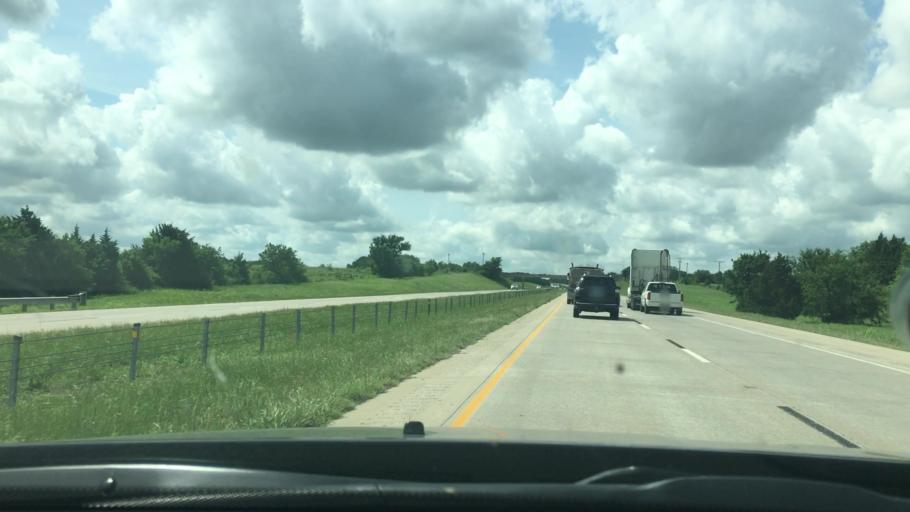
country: US
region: Oklahoma
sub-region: Love County
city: Marietta
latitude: 33.8572
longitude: -97.1343
